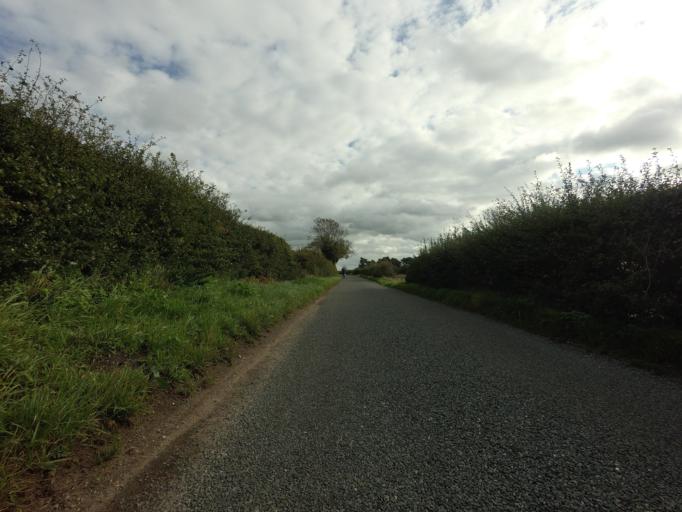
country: GB
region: England
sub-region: Norfolk
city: Dersingham
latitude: 52.8570
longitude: 0.5157
